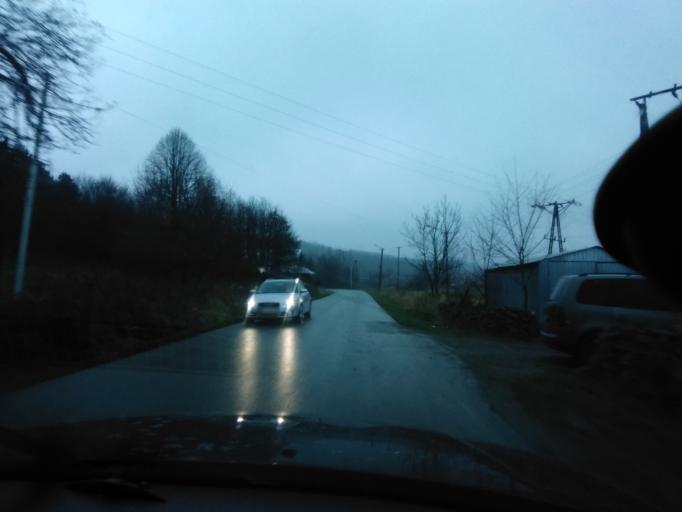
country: PL
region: Subcarpathian Voivodeship
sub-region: Powiat brzozowski
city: Jablonka
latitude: 49.7365
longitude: 22.1397
